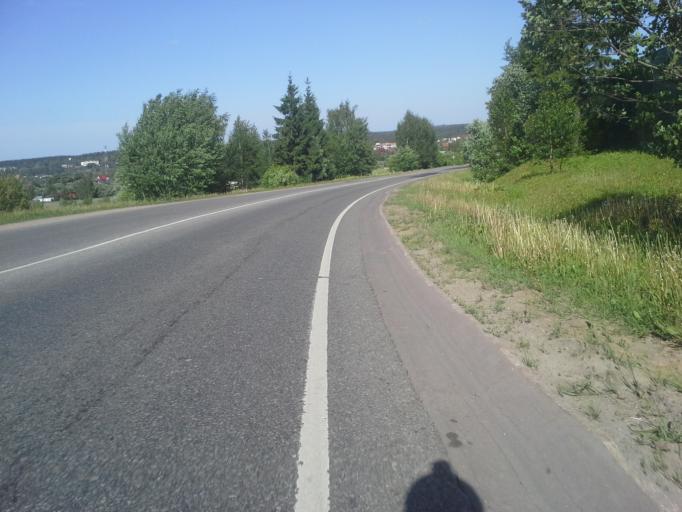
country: RU
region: Moskovskaya
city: Troitsk
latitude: 55.4295
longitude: 37.3071
